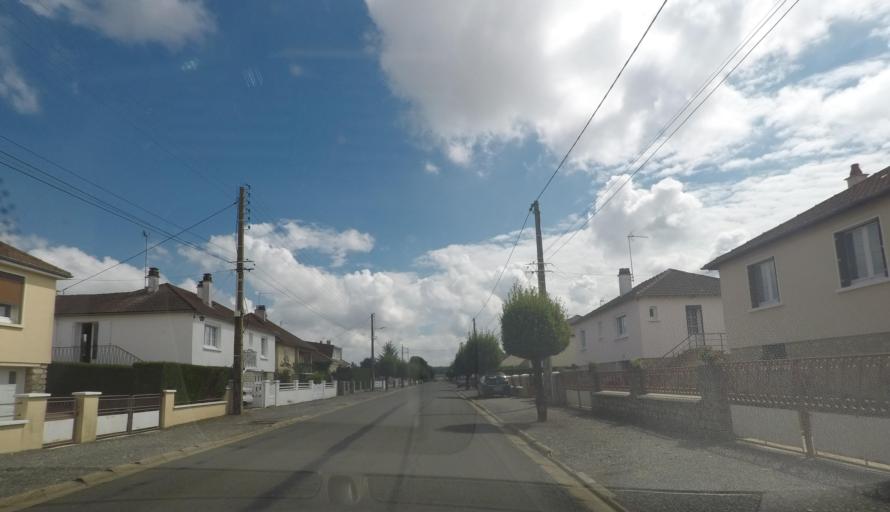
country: FR
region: Pays de la Loire
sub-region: Departement de la Sarthe
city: Saint-Cosme-en-Vairais
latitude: 48.2723
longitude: 0.4672
